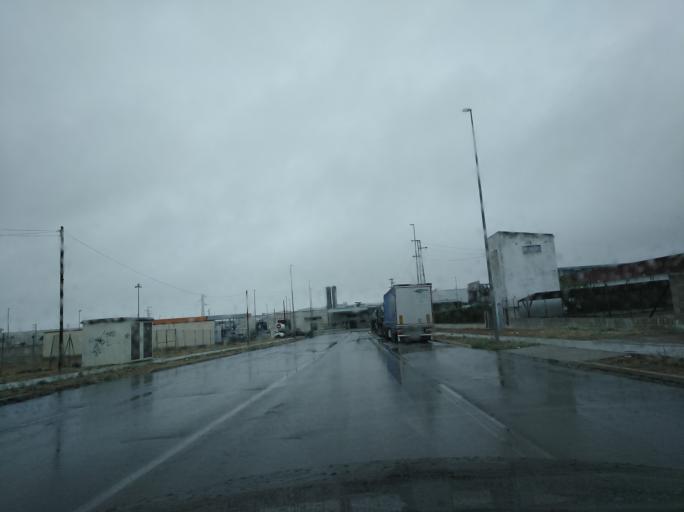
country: ES
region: Extremadura
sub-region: Provincia de Badajoz
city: Badajoz
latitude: 38.8951
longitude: -6.9865
